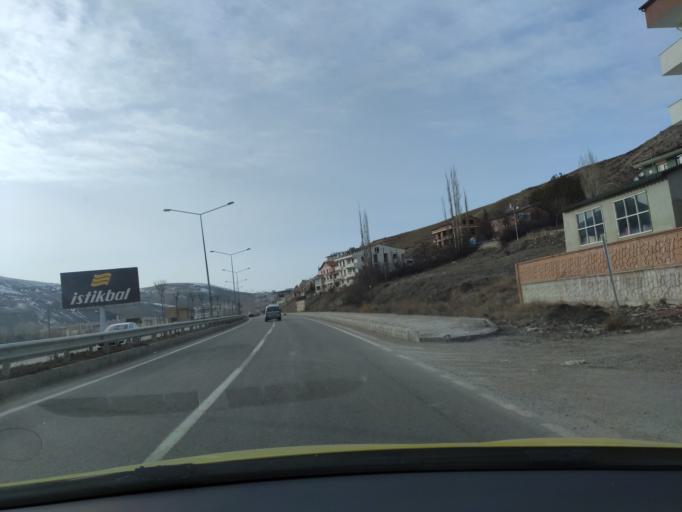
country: TR
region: Bayburt
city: Bayburt
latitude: 40.2431
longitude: 40.2424
